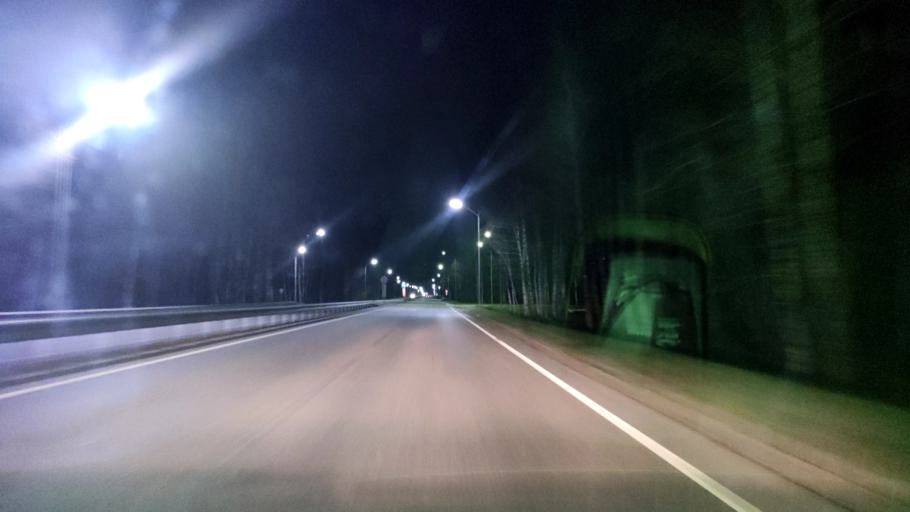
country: RU
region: Belgorod
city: Staryy Oskol
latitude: 51.4089
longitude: 37.8822
